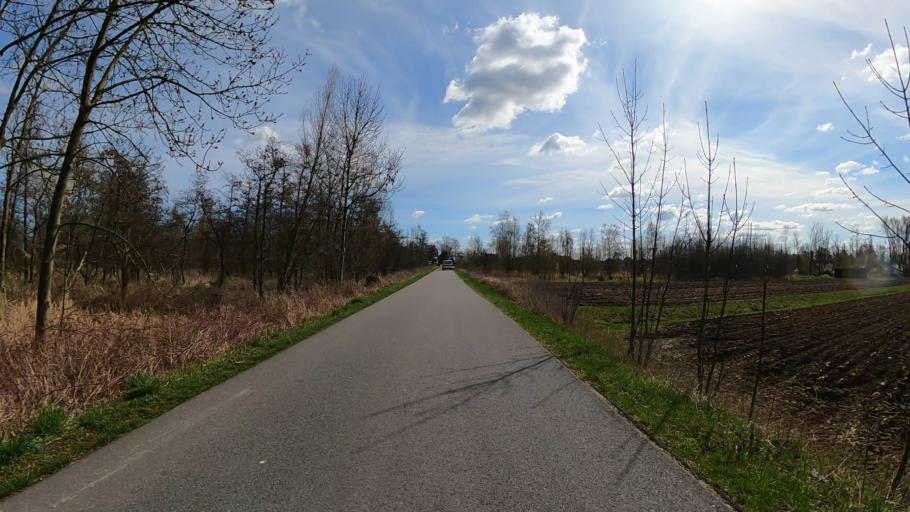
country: DE
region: Lower Saxony
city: Winsen
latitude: 53.4029
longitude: 10.2182
